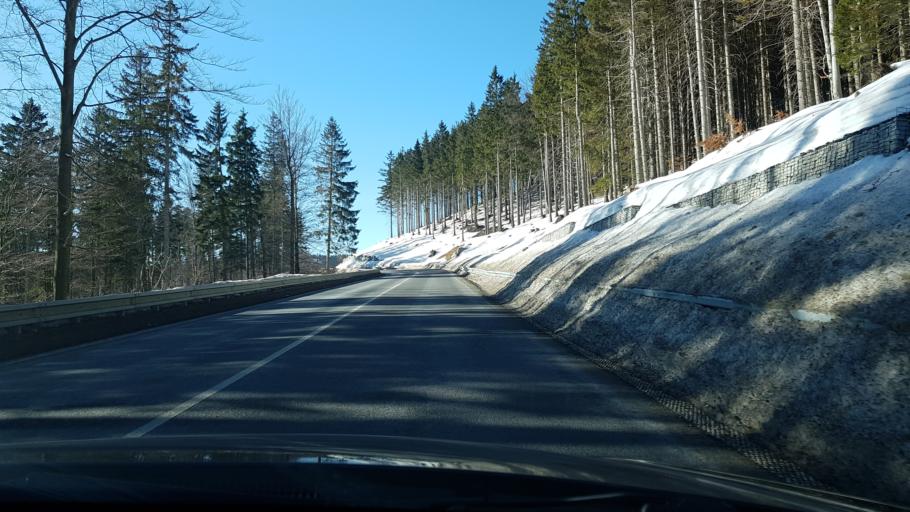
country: CZ
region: Olomoucky
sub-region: Okres Sumperk
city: Loucna nad Desnou
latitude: 50.1149
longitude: 17.1501
